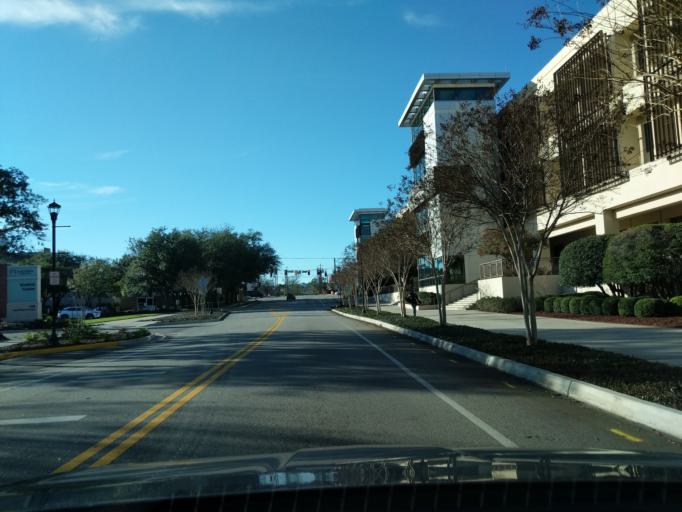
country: US
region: Georgia
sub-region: Richmond County
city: Augusta
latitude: 33.4698
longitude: -81.9905
